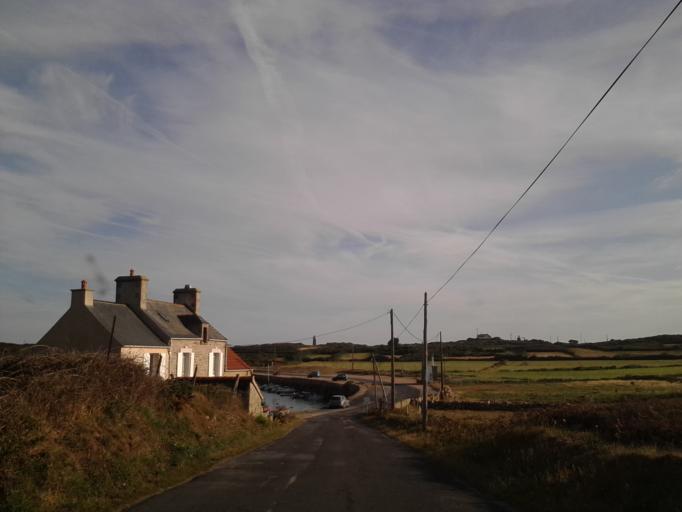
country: FR
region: Lower Normandy
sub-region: Departement de la Manche
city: Fermanville
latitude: 49.6857
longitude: -1.4725
